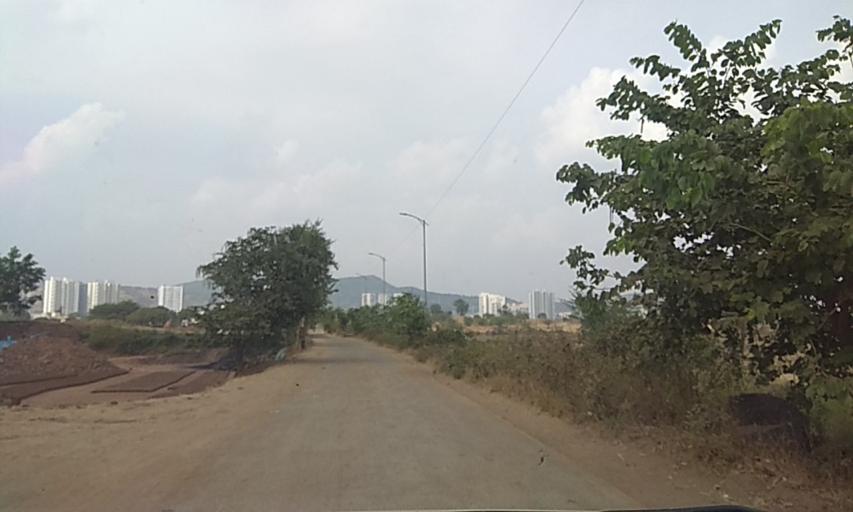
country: IN
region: Maharashtra
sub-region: Pune Division
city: Pimpri
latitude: 18.5791
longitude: 73.7081
